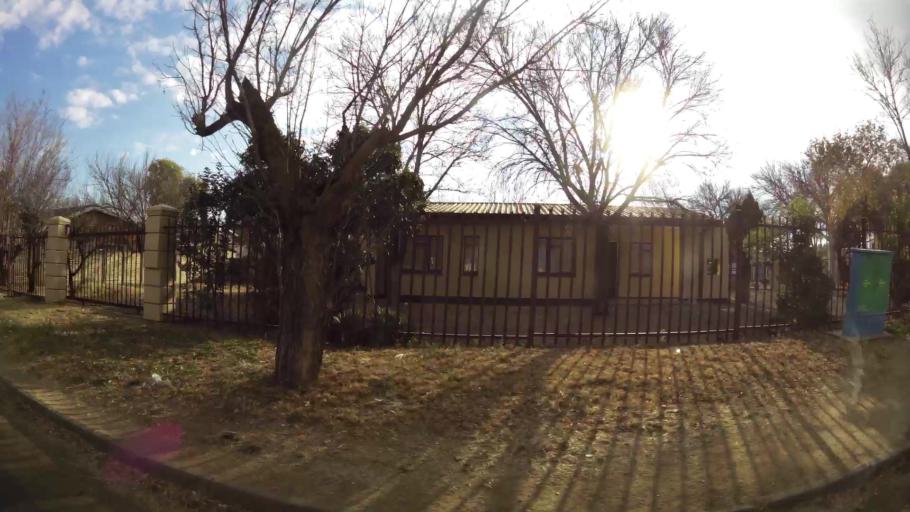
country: ZA
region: Orange Free State
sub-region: Mangaung Metropolitan Municipality
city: Bloemfontein
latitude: -29.1009
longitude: 26.1916
